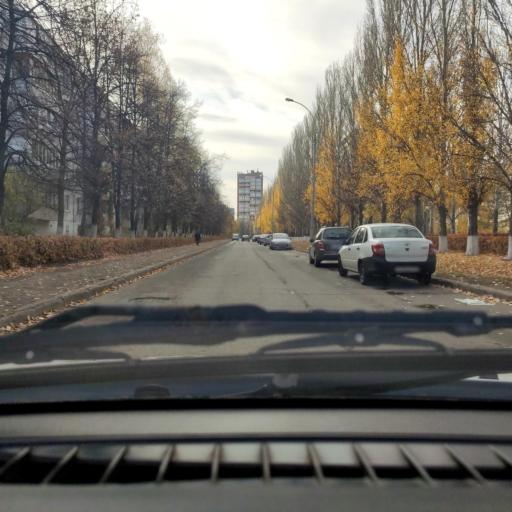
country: RU
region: Samara
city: Tol'yatti
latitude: 53.5302
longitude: 49.3043
